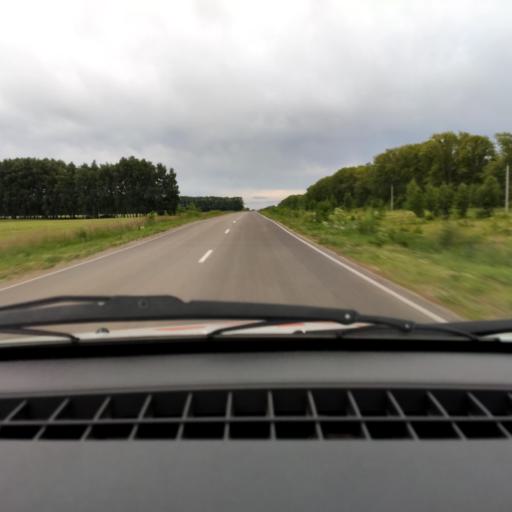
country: RU
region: Bashkortostan
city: Avdon
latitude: 54.5313
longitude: 55.7657
